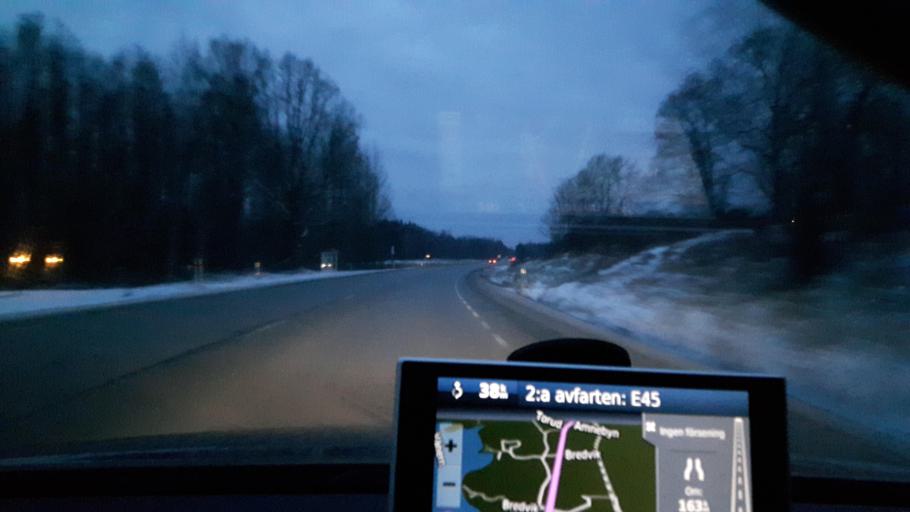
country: SE
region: Vaestra Goetaland
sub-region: Amals Kommun
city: Amal
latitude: 58.9981
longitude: 12.6806
